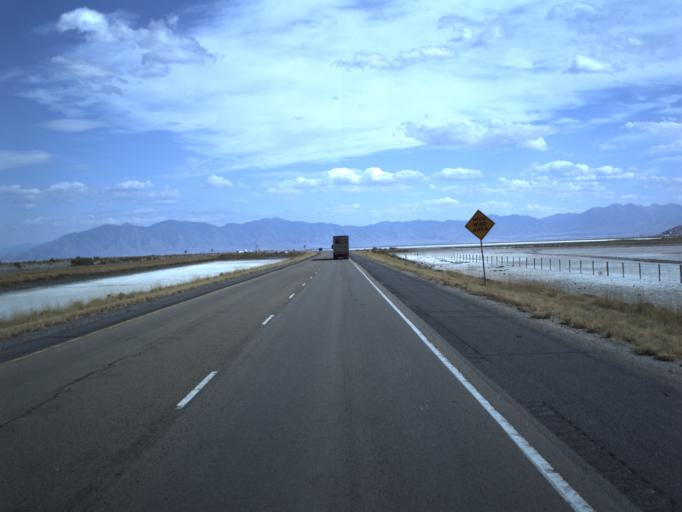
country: US
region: Utah
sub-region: Tooele County
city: Grantsville
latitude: 40.7417
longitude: -112.6288
